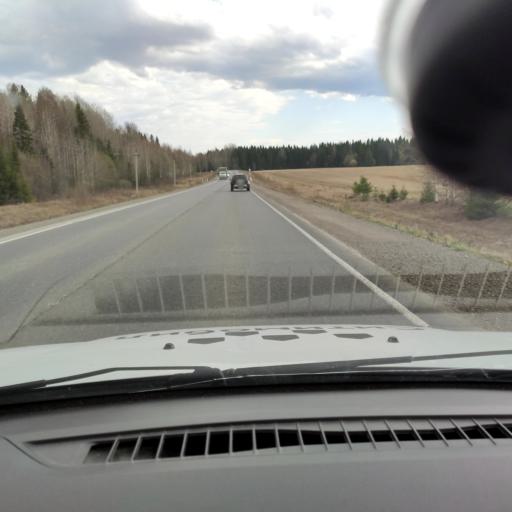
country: RU
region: Perm
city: Verkhnechusovskiye Gorodki
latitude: 58.2219
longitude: 57.1042
